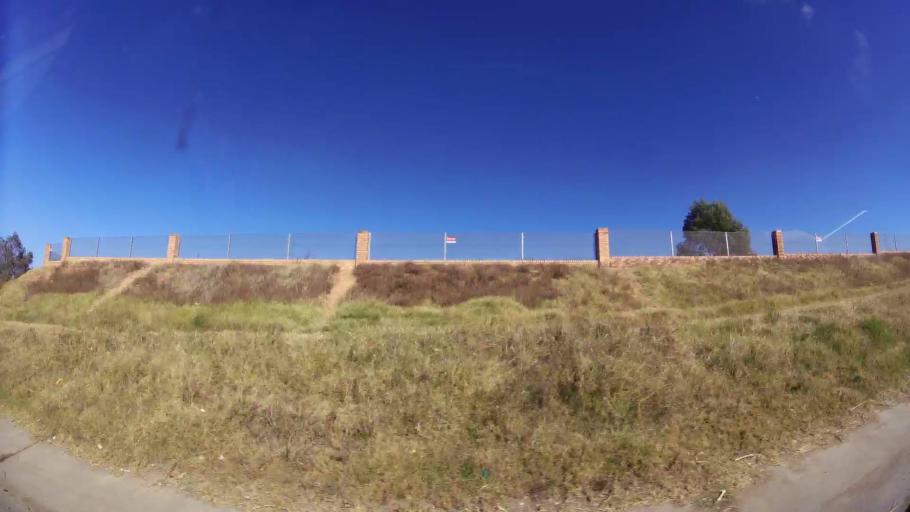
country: ZA
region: Gauteng
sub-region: City of Johannesburg Metropolitan Municipality
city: Diepsloot
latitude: -25.9091
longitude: 28.0894
